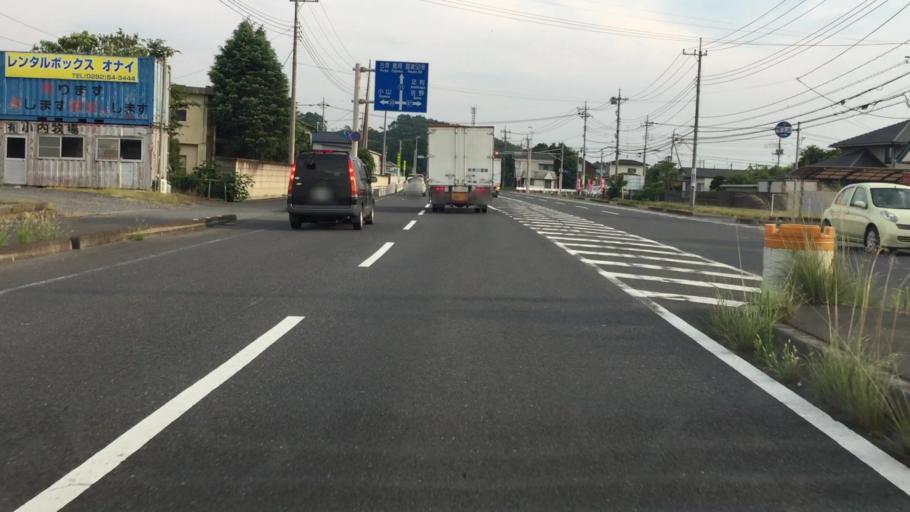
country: JP
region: Tochigi
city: Fujioka
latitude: 36.3203
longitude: 139.6768
